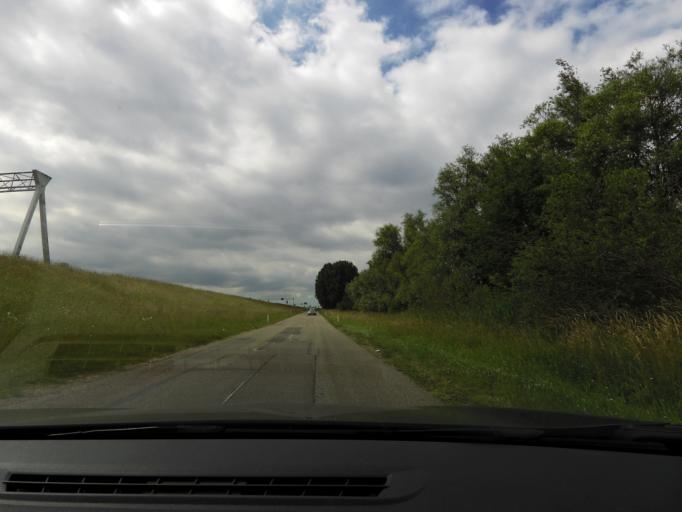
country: NL
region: North Brabant
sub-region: Gemeente Moerdijk
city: Willemstad
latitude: 51.6828
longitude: 4.4169
